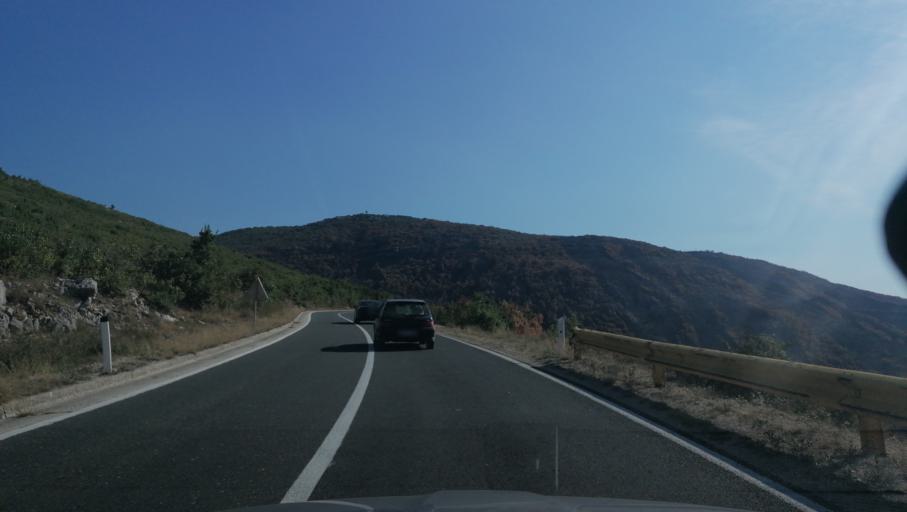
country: BA
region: Republika Srpska
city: Trebinje
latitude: 42.7199
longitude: 18.3854
